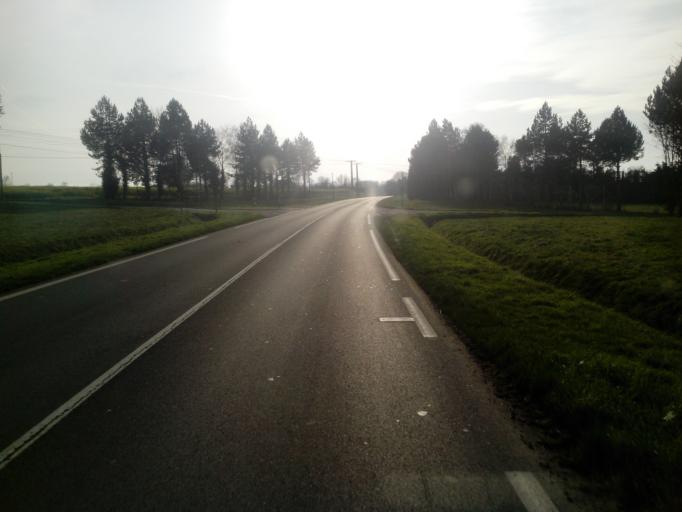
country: FR
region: Brittany
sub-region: Departement d'Ille-et-Vilaine
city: Gael
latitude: 48.1540
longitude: -2.2126
